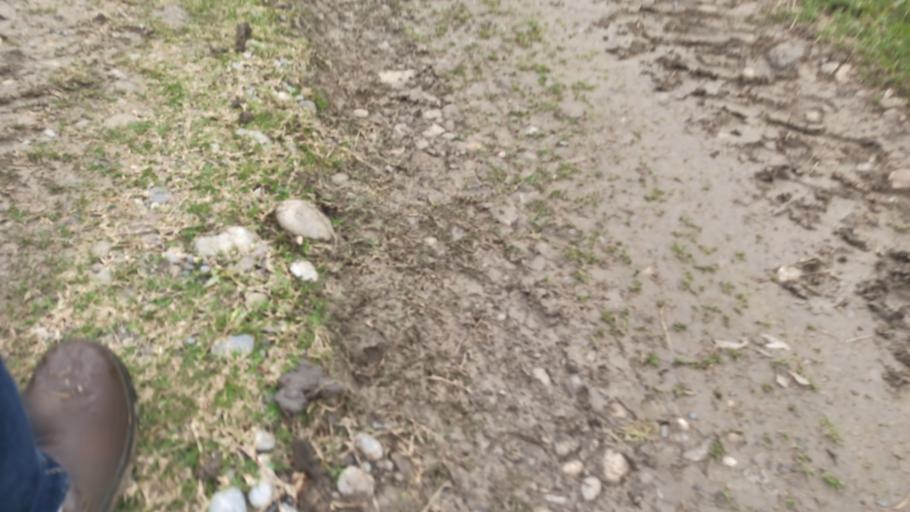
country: MX
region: Puebla
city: Espinal
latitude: 20.3024
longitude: -97.4103
